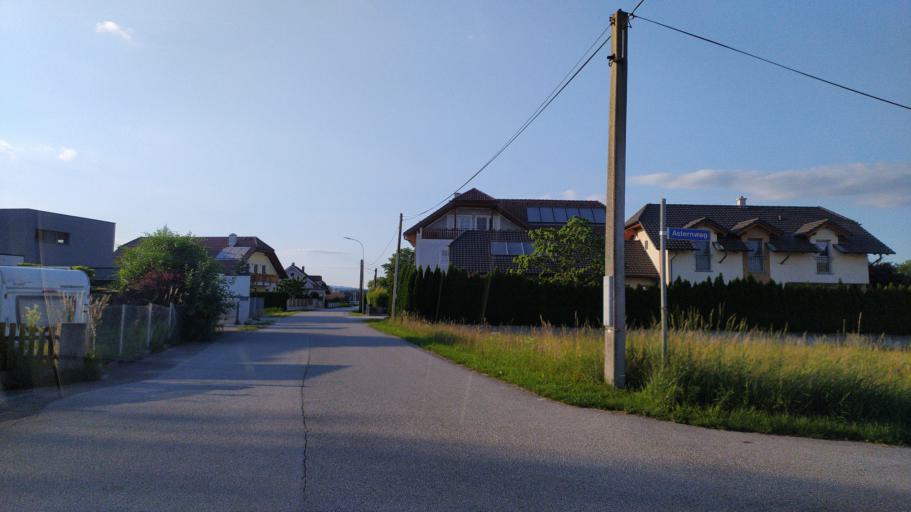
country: AT
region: Lower Austria
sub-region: Politischer Bezirk Amstetten
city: Ennsdorf
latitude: 48.2138
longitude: 14.5692
